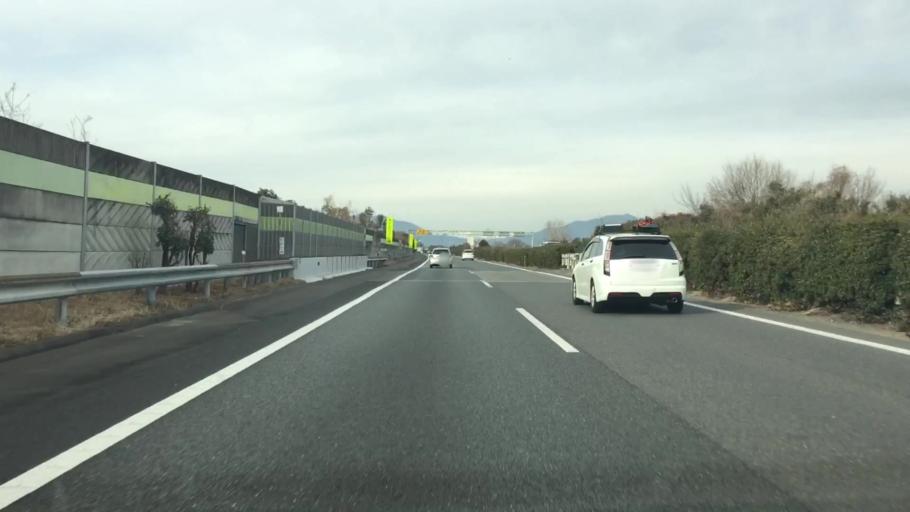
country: JP
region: Gunma
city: Kanekomachi
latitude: 36.4162
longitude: 139.0205
